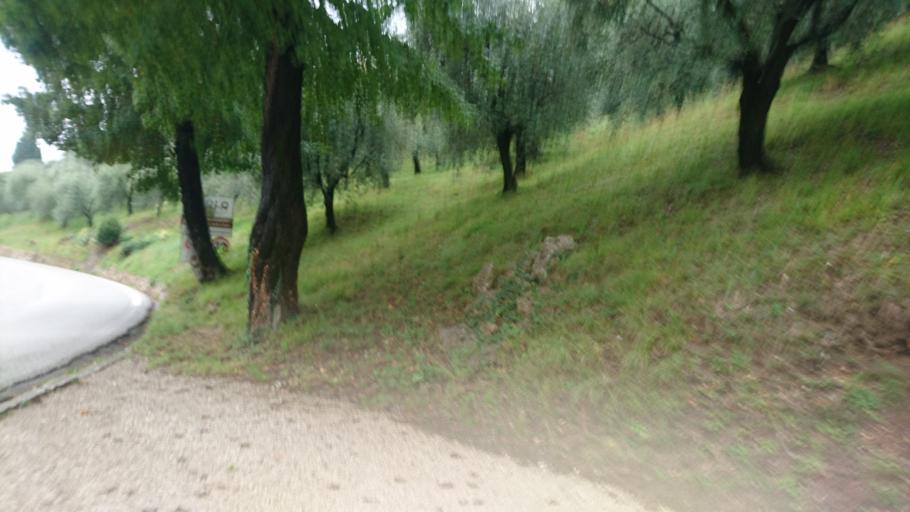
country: IT
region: Veneto
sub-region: Provincia di Treviso
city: Asolo
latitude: 45.8025
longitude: 11.9188
